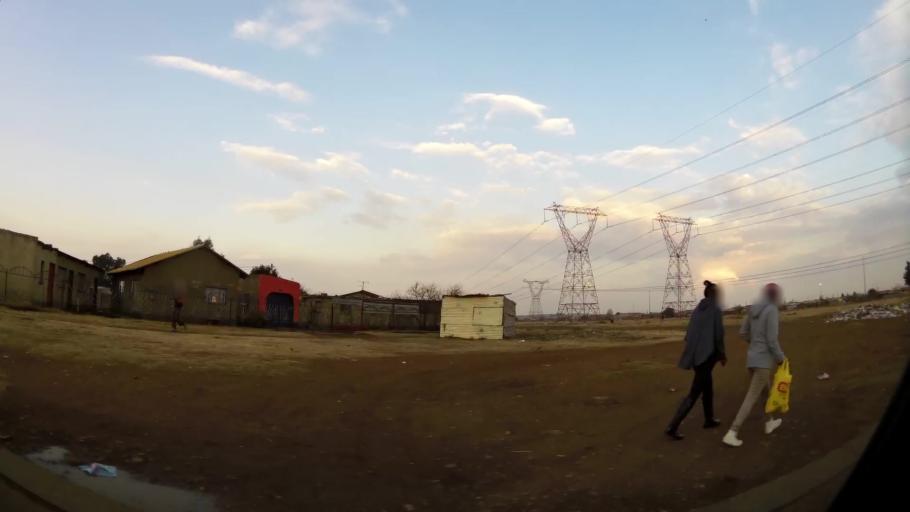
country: ZA
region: Gauteng
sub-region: City of Johannesburg Metropolitan Municipality
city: Orange Farm
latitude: -26.5555
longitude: 27.8395
